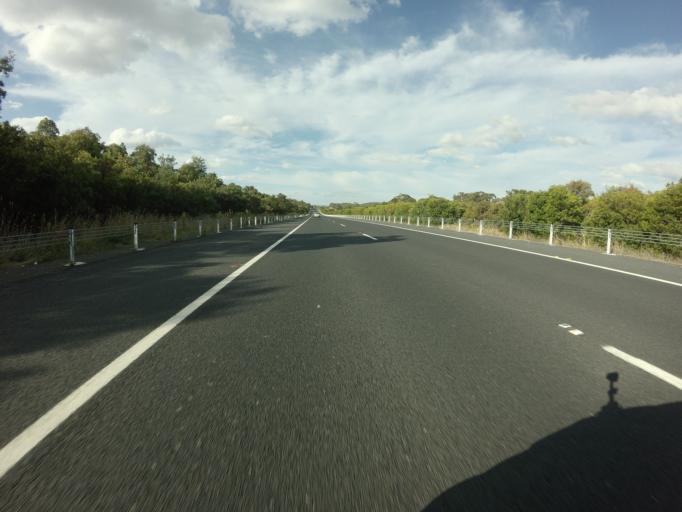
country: AU
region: Australian Capital Territory
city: Kaleen
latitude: -35.1898
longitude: 149.2255
